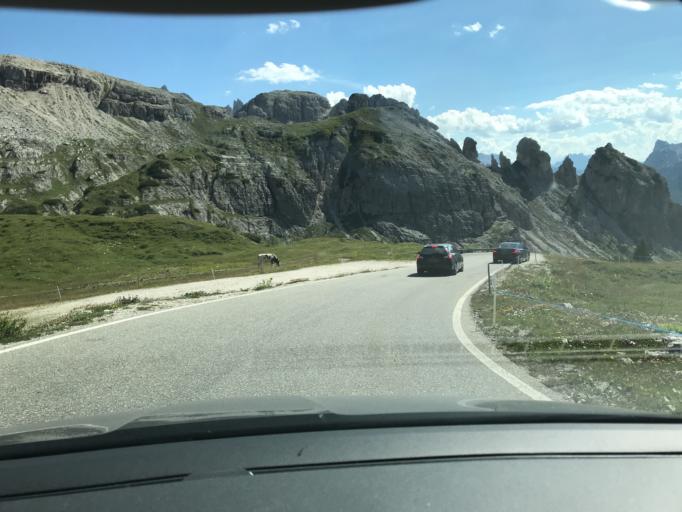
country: IT
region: Trentino-Alto Adige
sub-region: Bolzano
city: Sesto
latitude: 46.6083
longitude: 12.2948
